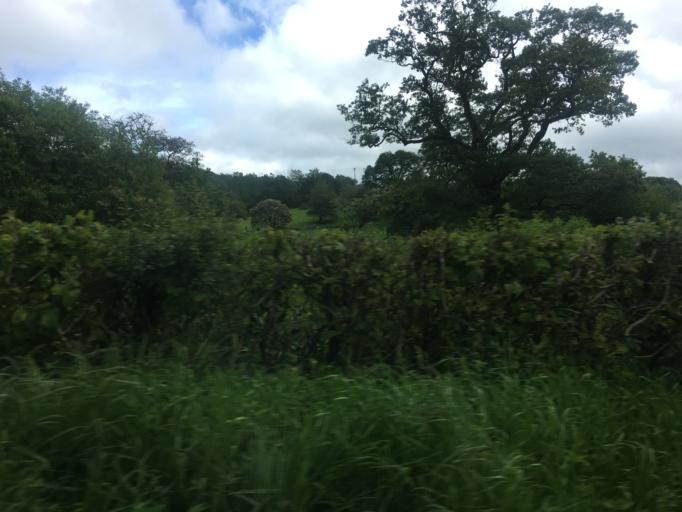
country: GB
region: Wales
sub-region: County of Ceredigion
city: Lampeter
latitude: 52.1249
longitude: -4.0772
